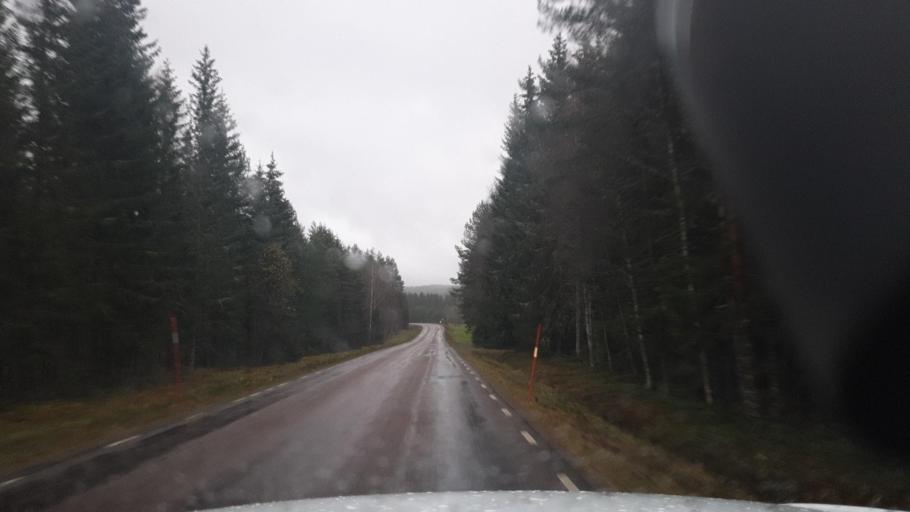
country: SE
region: Vaermland
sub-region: Eda Kommun
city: Amotfors
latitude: 59.7348
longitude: 12.1693
